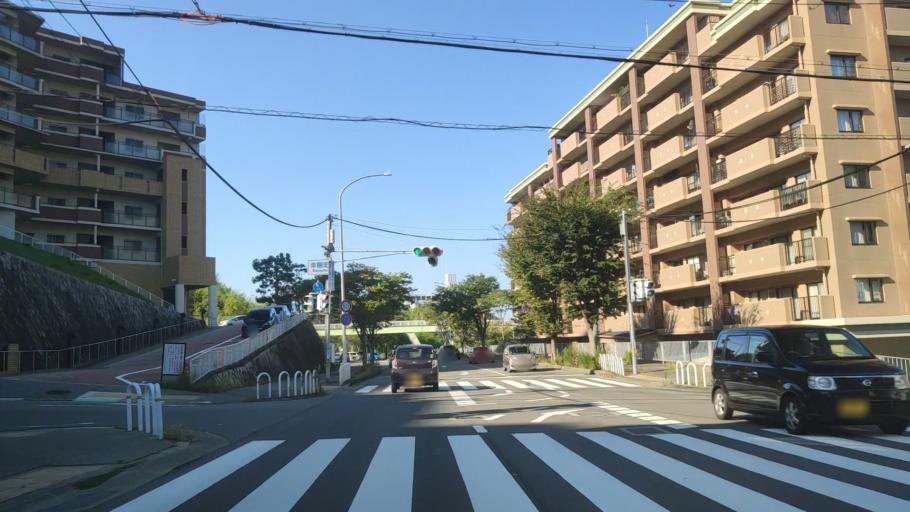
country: JP
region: Hyogo
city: Kobe
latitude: 34.7689
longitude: 135.1876
